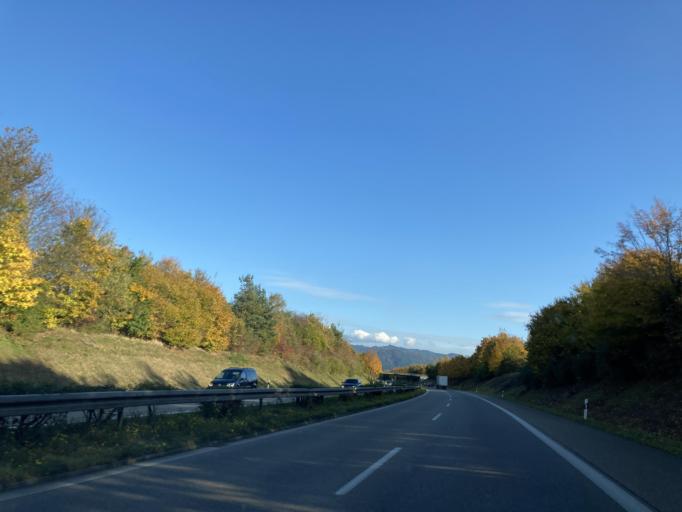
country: DE
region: Baden-Wuerttemberg
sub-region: Freiburg Region
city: Kirchzarten
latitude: 47.9755
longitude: 7.9203
